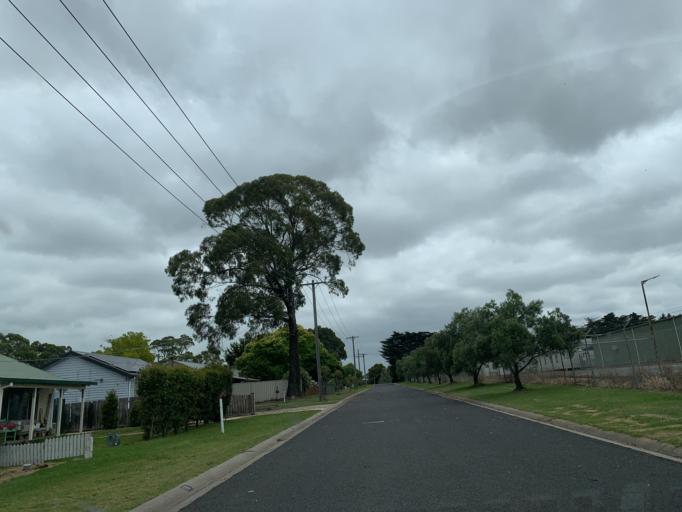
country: AU
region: Victoria
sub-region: Wellington
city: Heyfield
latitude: -37.9792
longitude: 146.7965
